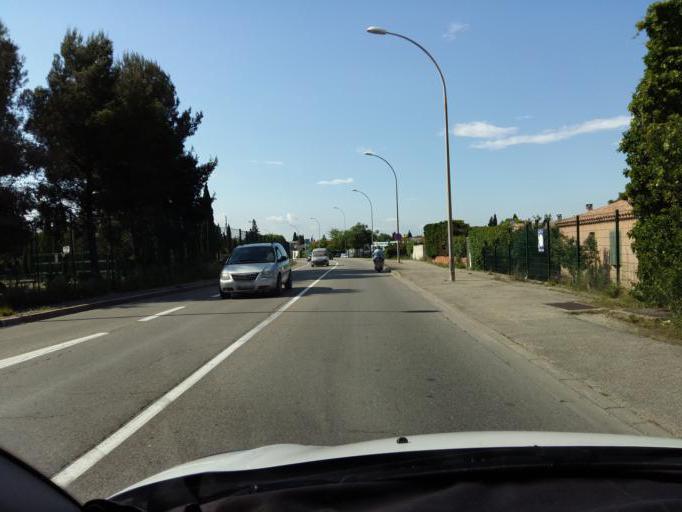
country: FR
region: Provence-Alpes-Cote d'Azur
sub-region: Departement du Vaucluse
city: Cavaillon
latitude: 43.8456
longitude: 5.0434
